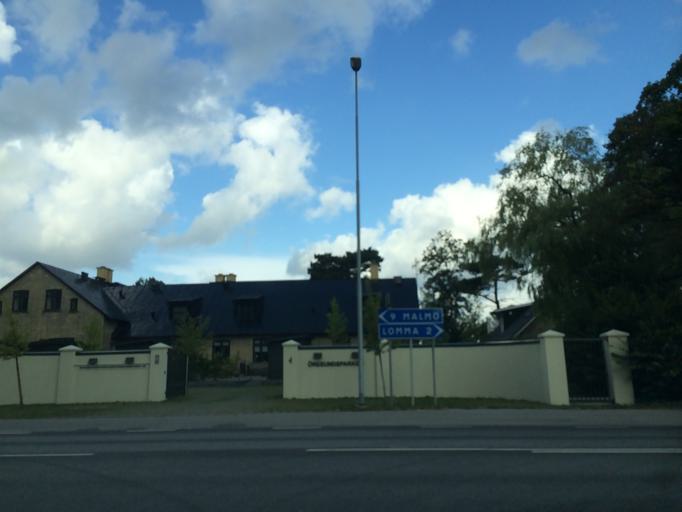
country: SE
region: Skane
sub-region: Lomma Kommun
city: Lomma
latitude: 55.6568
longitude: 13.0569
